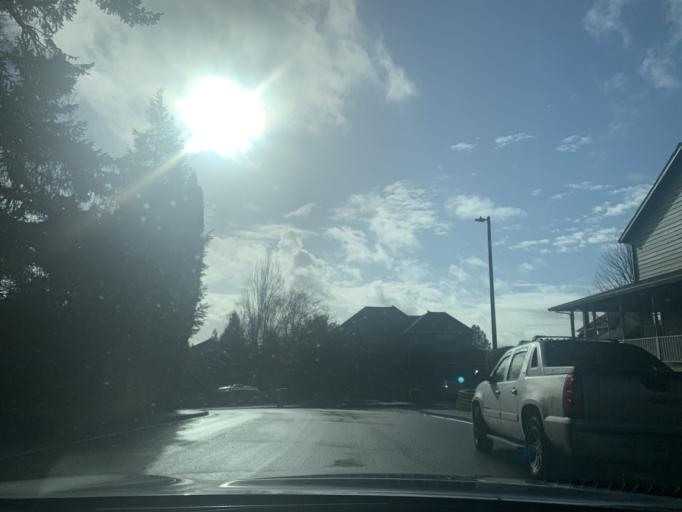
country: US
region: Oregon
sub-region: Washington County
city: King City
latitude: 45.4038
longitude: -122.8279
